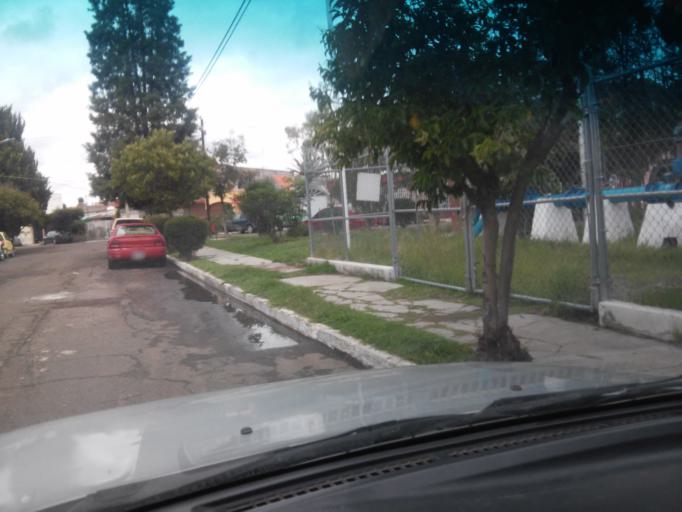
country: MX
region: Durango
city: Victoria de Durango
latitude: 24.0179
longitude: -104.6400
